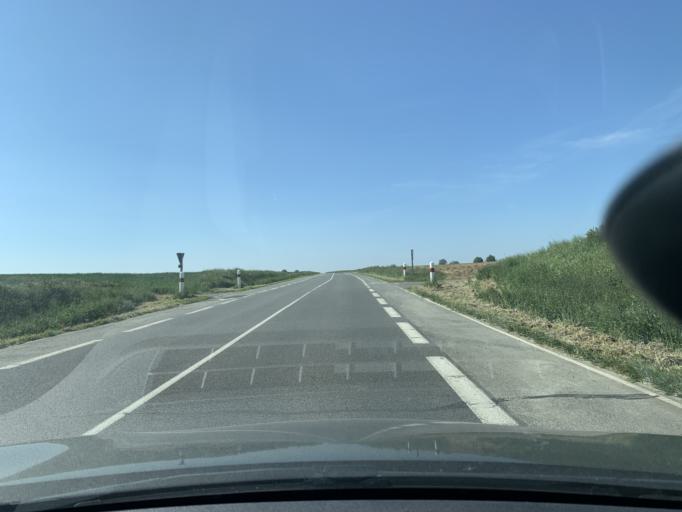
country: FR
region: Nord-Pas-de-Calais
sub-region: Departement du Nord
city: Rumilly-en-Cambresis
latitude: 50.1241
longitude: 3.2462
